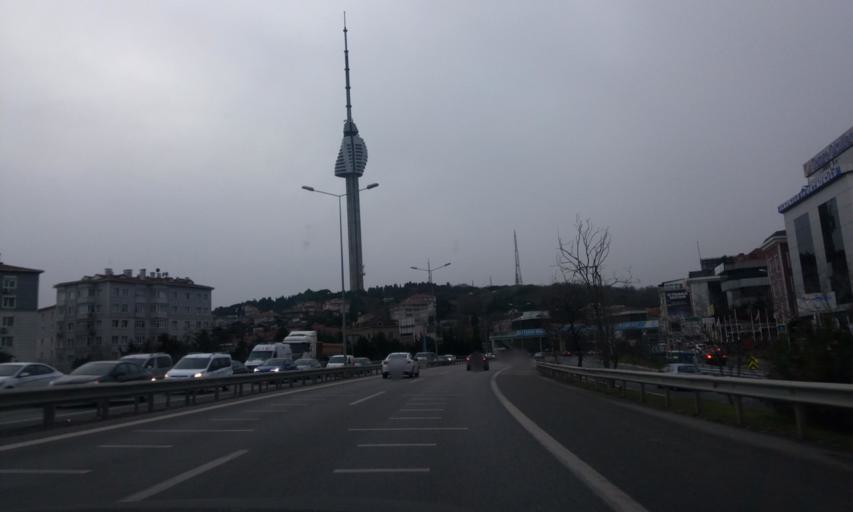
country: TR
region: Istanbul
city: UEskuedar
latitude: 41.0202
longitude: 29.0734
